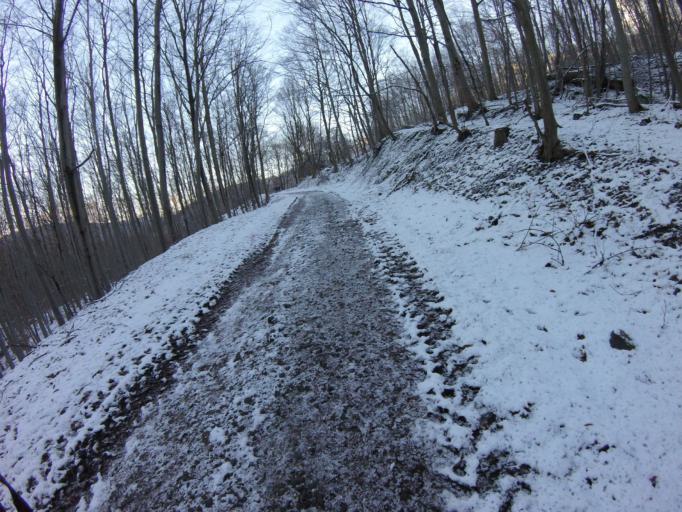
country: HU
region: Pest
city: Pilisszentkereszt
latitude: 47.7298
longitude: 18.8933
